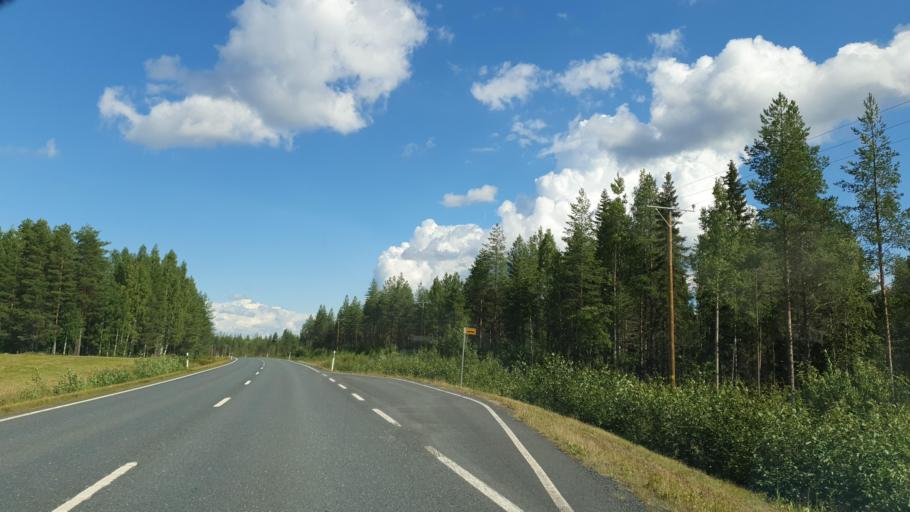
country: FI
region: Kainuu
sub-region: Kehys-Kainuu
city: Kuhmo
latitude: 64.0839
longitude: 29.0606
